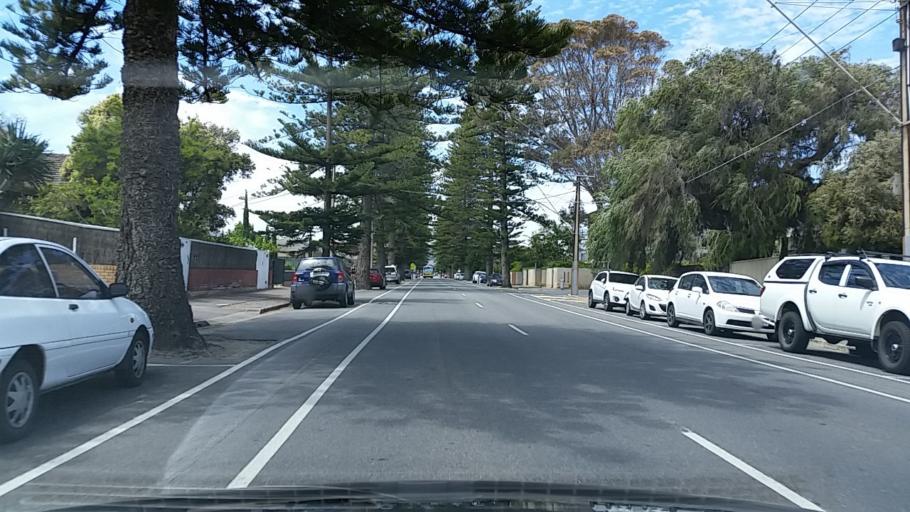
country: AU
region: South Australia
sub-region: Adelaide
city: Glenelg
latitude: -34.9853
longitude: 138.5145
